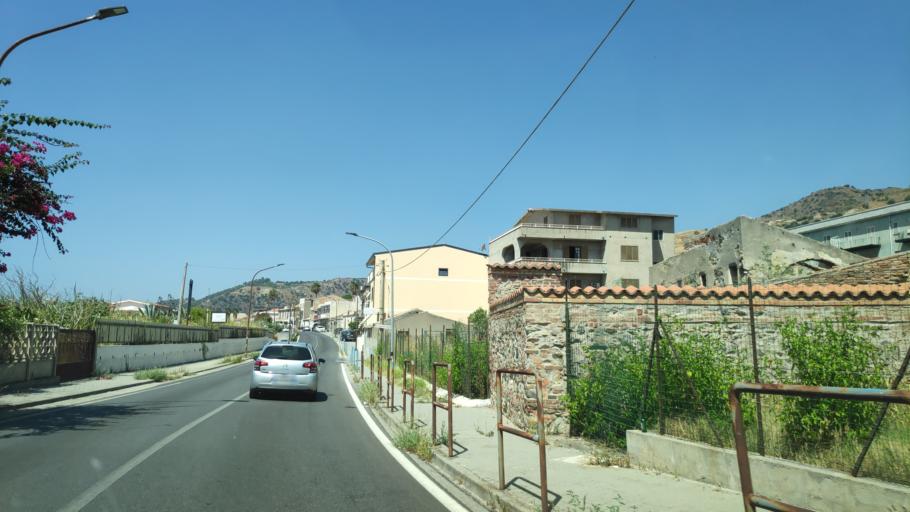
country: IT
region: Calabria
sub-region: Provincia di Reggio Calabria
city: Palizzi Marina
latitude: 37.9179
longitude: 15.9947
